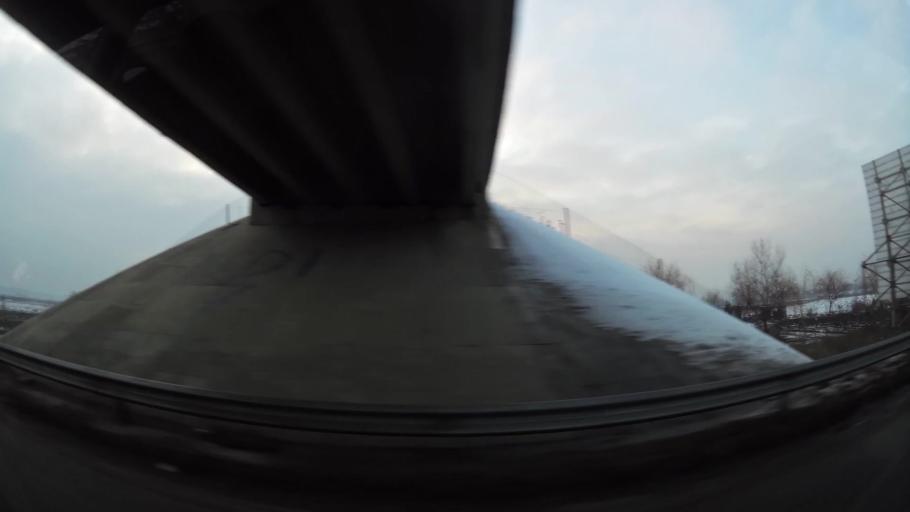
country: MK
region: Aracinovo
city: Arachinovo
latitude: 42.0073
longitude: 21.5350
